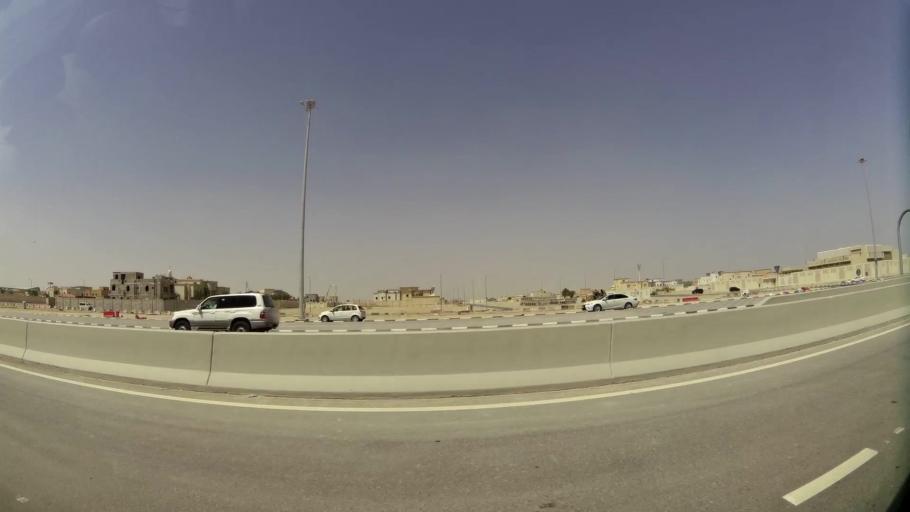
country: QA
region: Baladiyat Umm Salal
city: Umm Salal Muhammad
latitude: 25.3837
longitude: 51.4503
